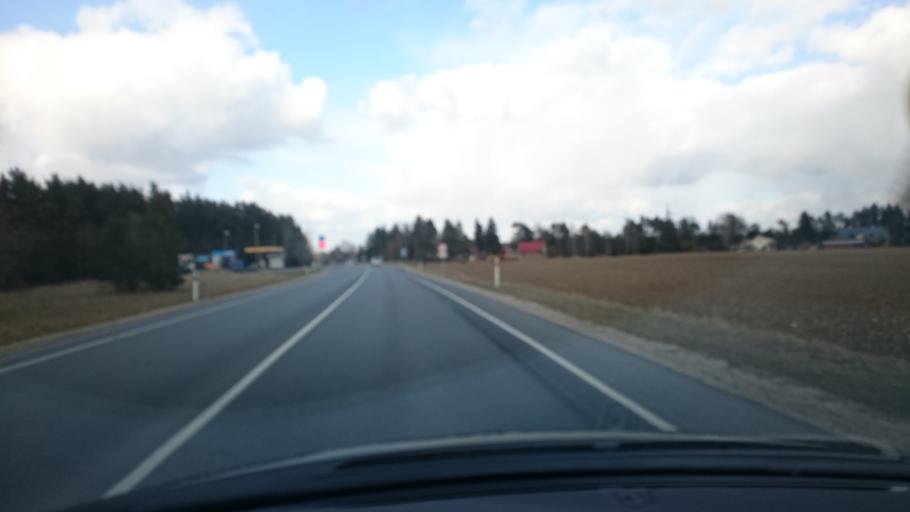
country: EE
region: Harju
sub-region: Nissi vald
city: Riisipere
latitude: 59.1219
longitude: 24.3006
